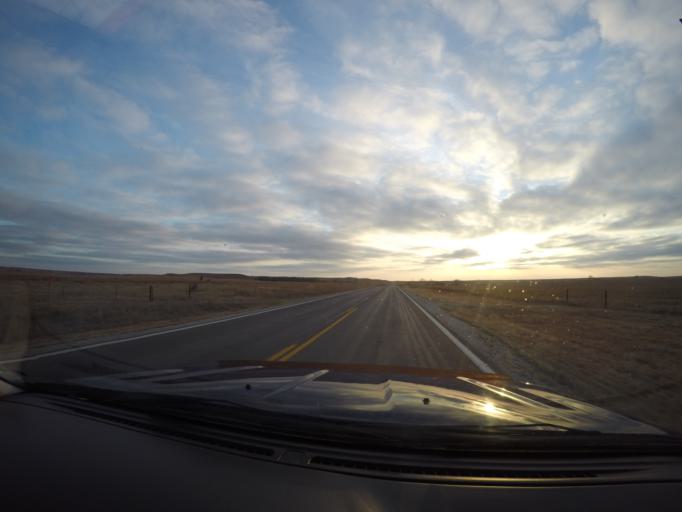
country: US
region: Kansas
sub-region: Morris County
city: Council Grove
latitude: 38.5904
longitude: -96.5064
